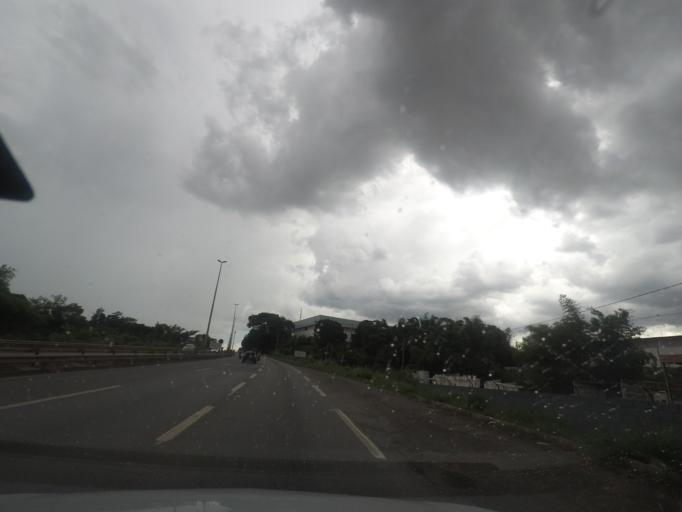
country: BR
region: Goias
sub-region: Goiania
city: Goiania
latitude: -16.6838
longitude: -49.2342
